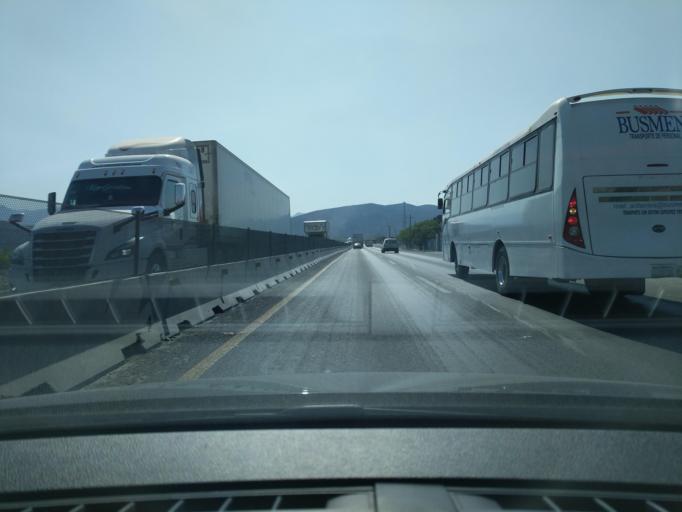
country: MX
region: Nuevo Leon
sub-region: Garcia
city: Los Parques
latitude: 25.7697
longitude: -100.4788
